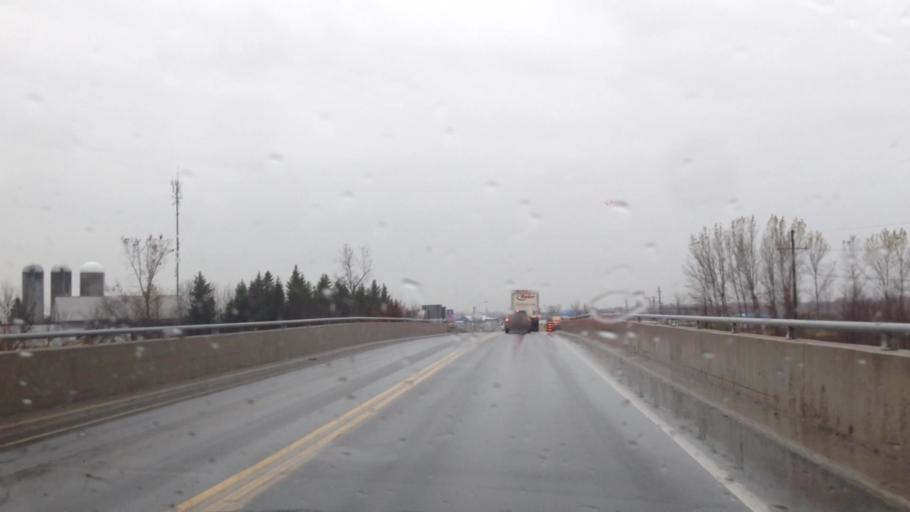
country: CA
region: Ontario
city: Bourget
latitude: 45.3367
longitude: -75.3452
